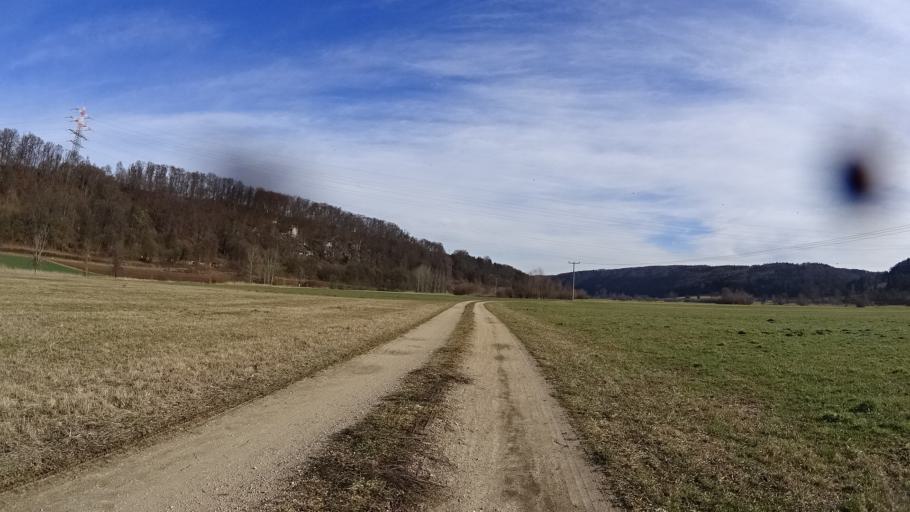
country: DE
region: Bavaria
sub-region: Upper Bavaria
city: Walting
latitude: 48.8980
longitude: 11.2792
